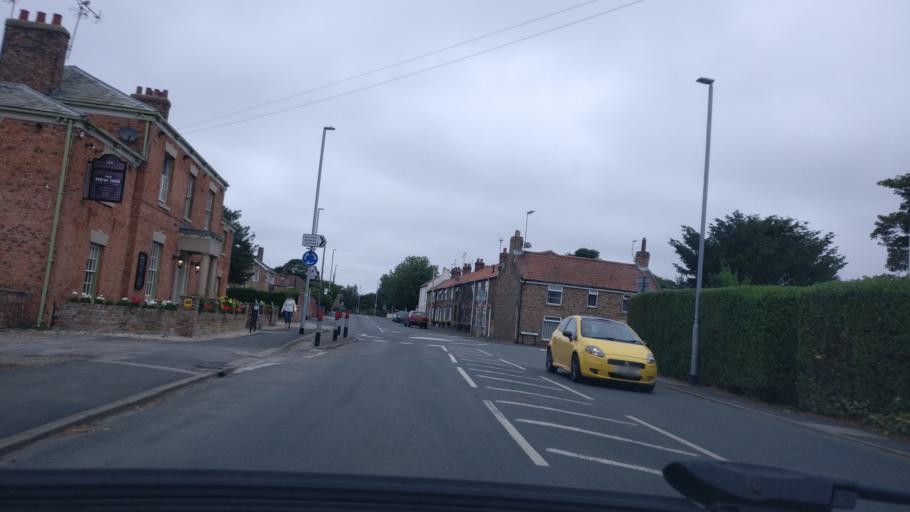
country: GB
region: England
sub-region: East Riding of Yorkshire
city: Leven
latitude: 53.8891
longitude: -0.3161
